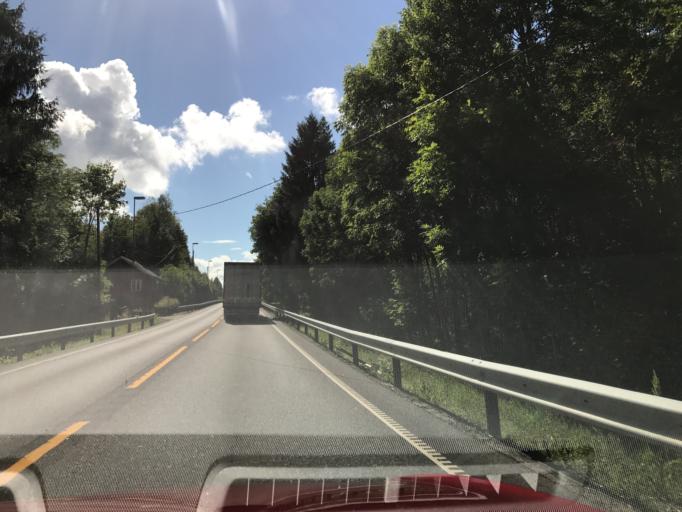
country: NO
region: Telemark
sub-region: Bamble
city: Herre
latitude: 58.9697
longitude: 9.5666
